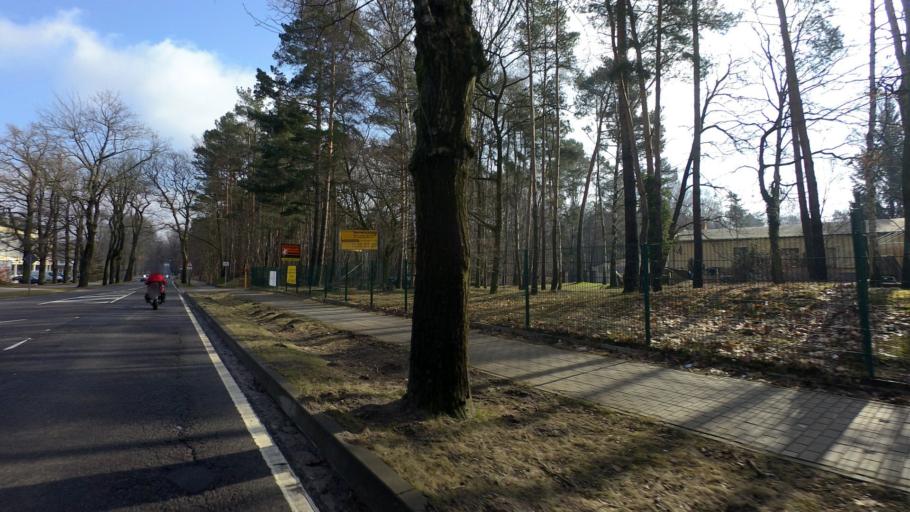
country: DE
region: Brandenburg
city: Glienicke
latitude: 52.6425
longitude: 13.3205
